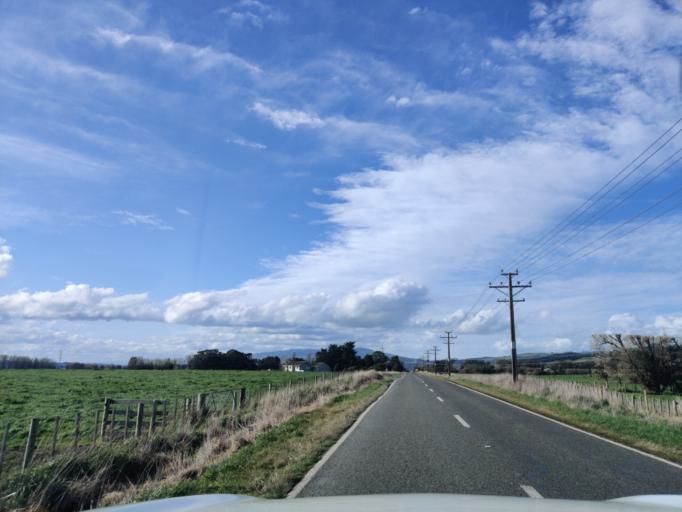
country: NZ
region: Manawatu-Wanganui
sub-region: Palmerston North City
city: Palmerston North
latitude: -40.3474
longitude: 175.7044
